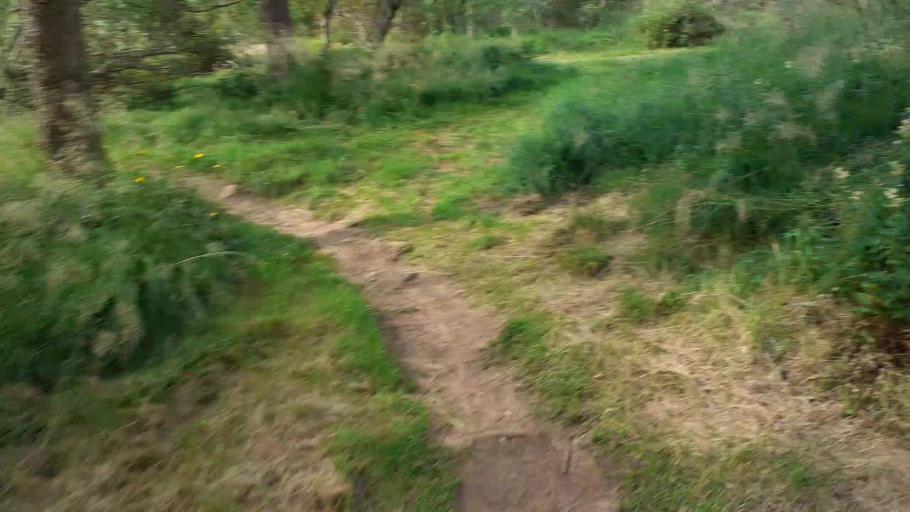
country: IS
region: Northeast
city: Akureyri
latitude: 65.6404
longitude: -18.0868
